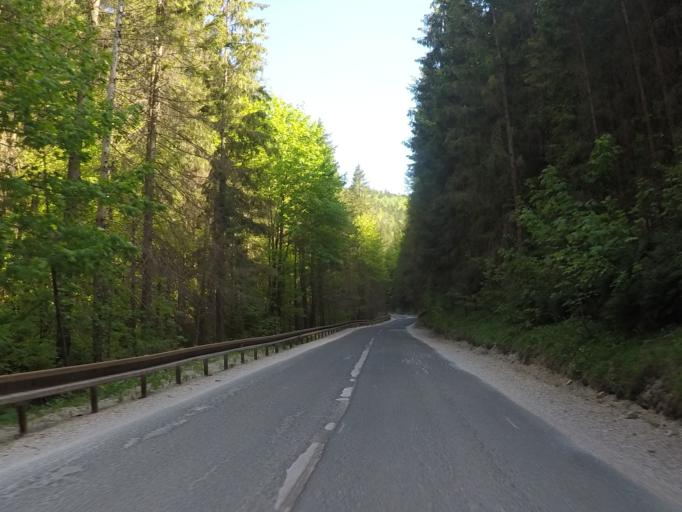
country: SK
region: Kosicky
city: Dobsina
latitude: 48.8662
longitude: 20.3484
